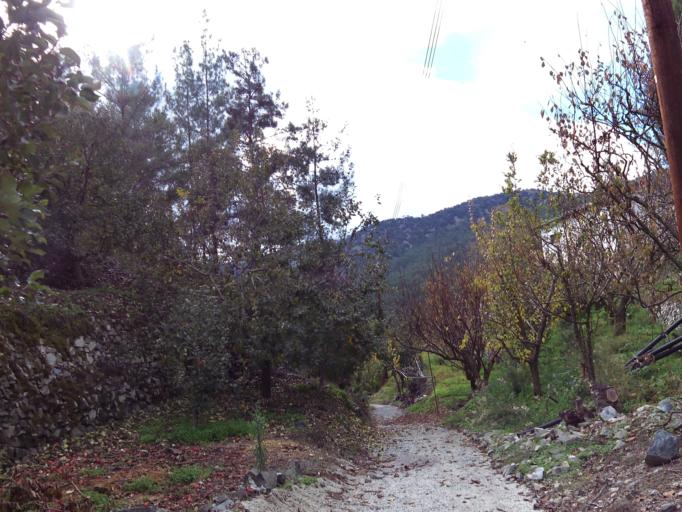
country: CY
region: Limassol
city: Kyperounta
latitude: 34.9321
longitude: 32.9386
